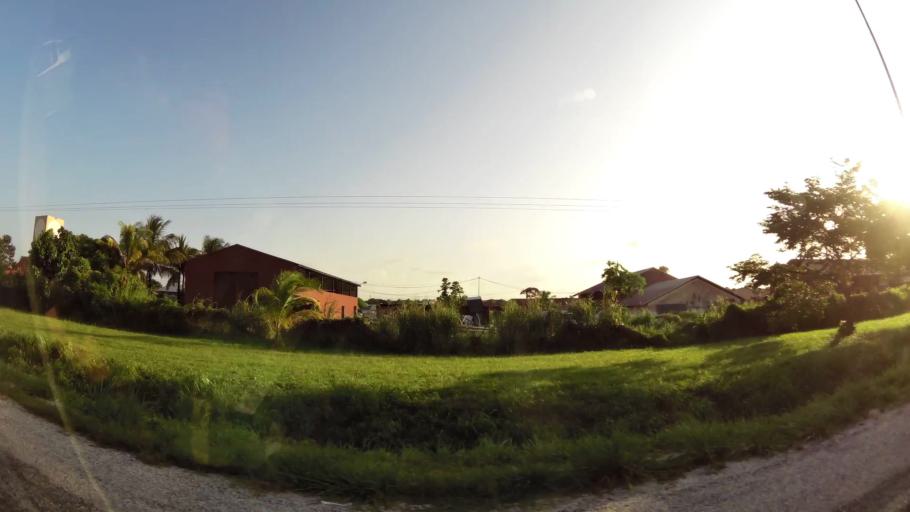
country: GF
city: Macouria
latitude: 5.0160
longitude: -52.4764
